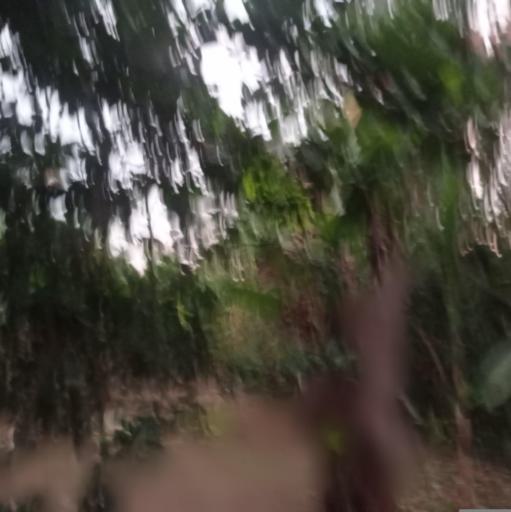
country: BO
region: La Paz
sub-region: Provincia Larecaja
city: Guanay
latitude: -15.5675
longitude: -67.3295
